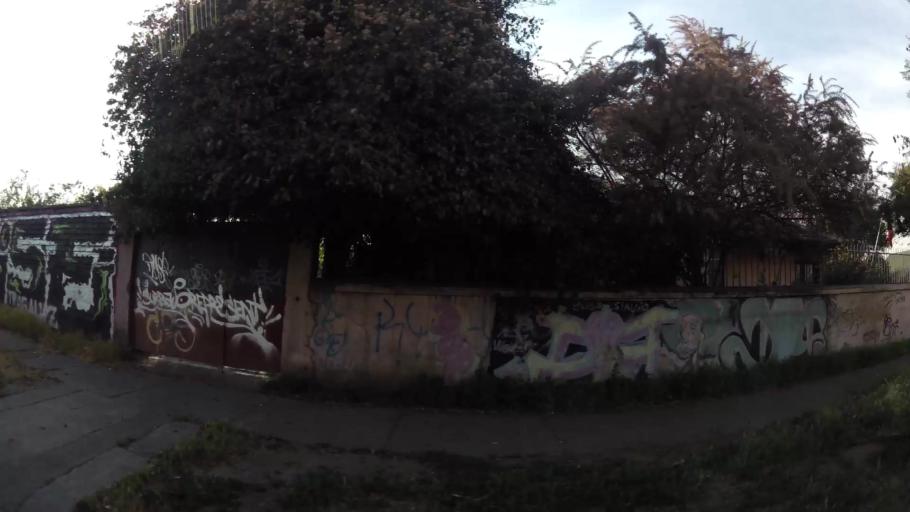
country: CL
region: Santiago Metropolitan
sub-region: Provincia de Santiago
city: Santiago
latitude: -33.5175
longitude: -70.6635
